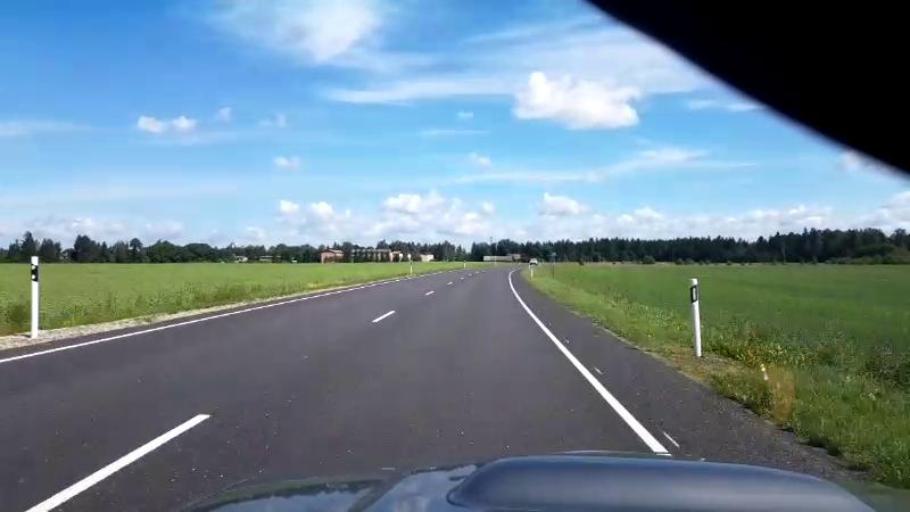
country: EE
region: Jaervamaa
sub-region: Jaerva-Jaani vald
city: Jarva-Jaani
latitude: 59.1221
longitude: 25.7370
